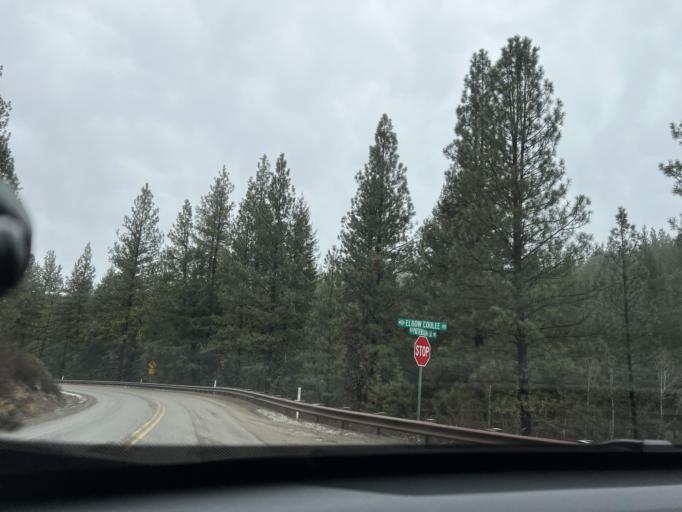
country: US
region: Washington
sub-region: Chelan County
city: Granite Falls
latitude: 48.4348
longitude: -120.2253
